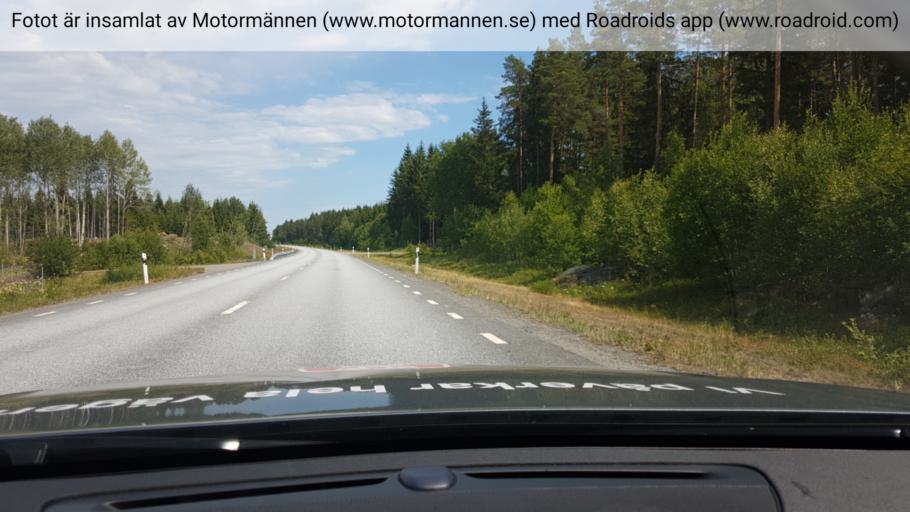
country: SE
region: Uppsala
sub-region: Osthammars Kommun
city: Gimo
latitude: 60.1643
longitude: 18.2497
